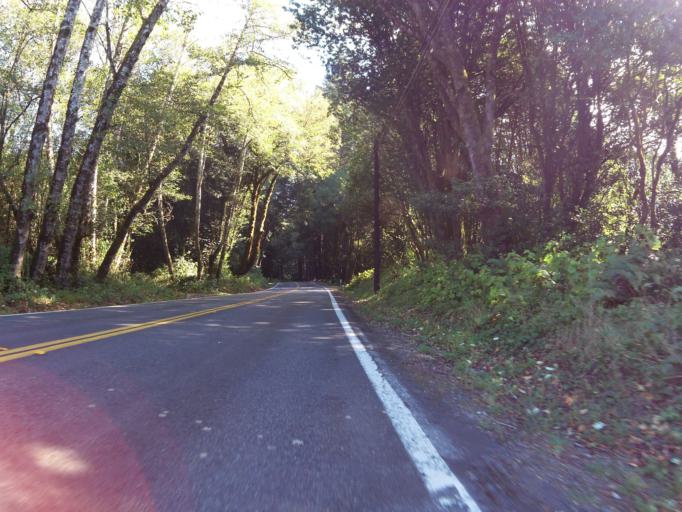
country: US
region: California
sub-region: Del Norte County
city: Bertsch-Oceanview
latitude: 41.8468
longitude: -124.1171
